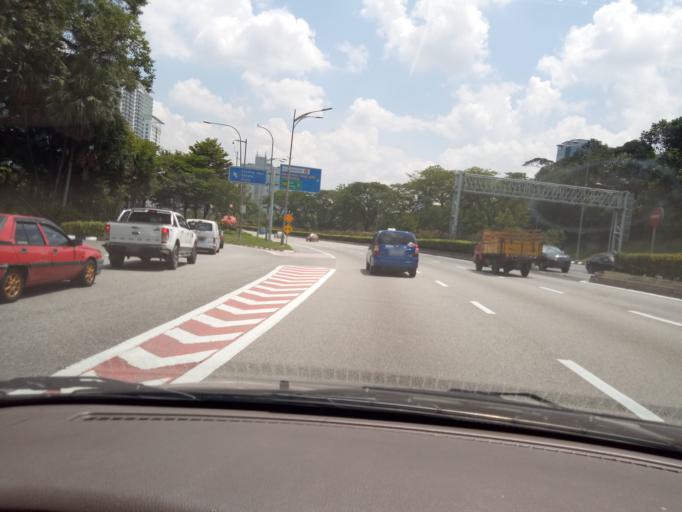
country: MY
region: Kuala Lumpur
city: Kuala Lumpur
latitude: 3.1345
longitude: 101.6970
